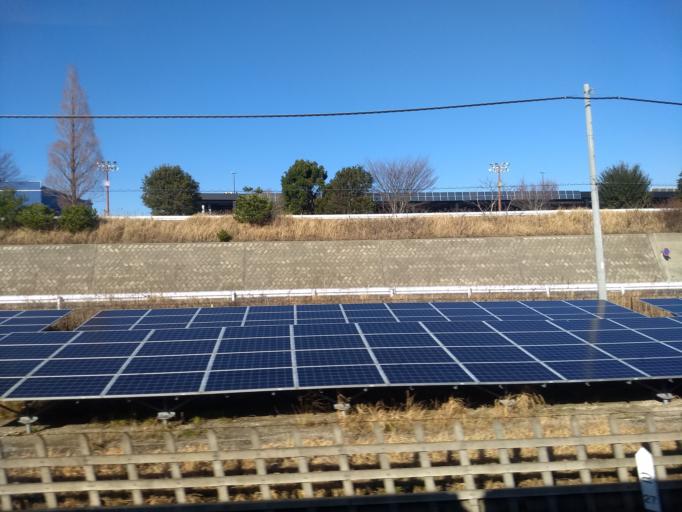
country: JP
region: Chiba
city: Shiroi
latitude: 35.8057
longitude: 140.1537
